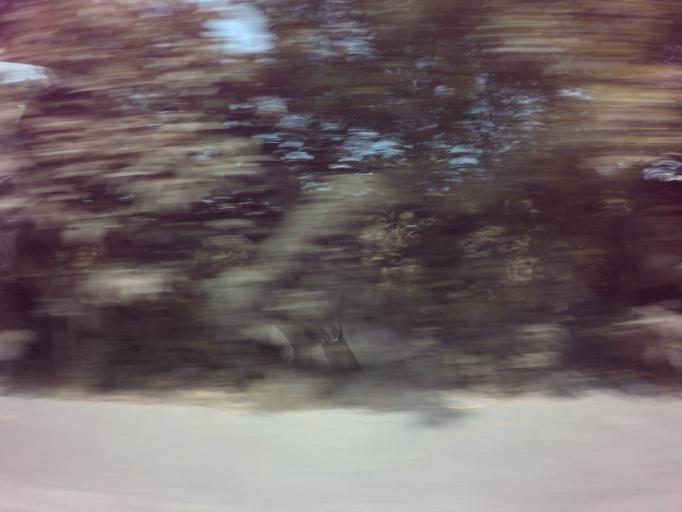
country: PH
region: Calabarzon
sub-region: Province of Rizal
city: Pateros
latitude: 14.5447
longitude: 121.0888
